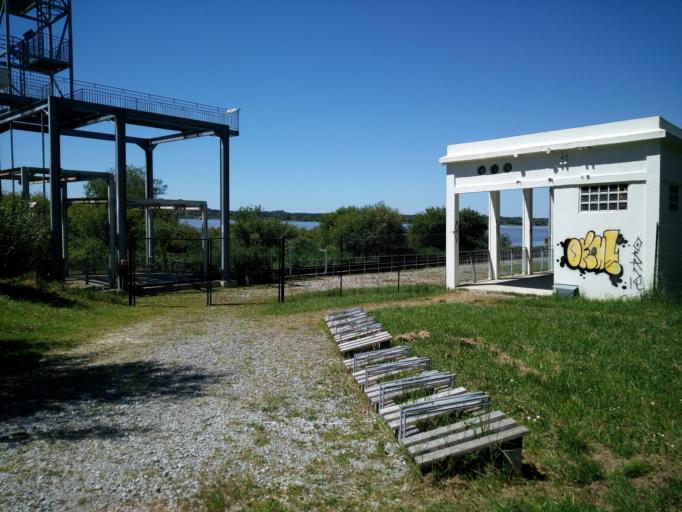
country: FR
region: Aquitaine
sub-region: Departement des Landes
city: Labenne
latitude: 43.5811
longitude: -1.3904
